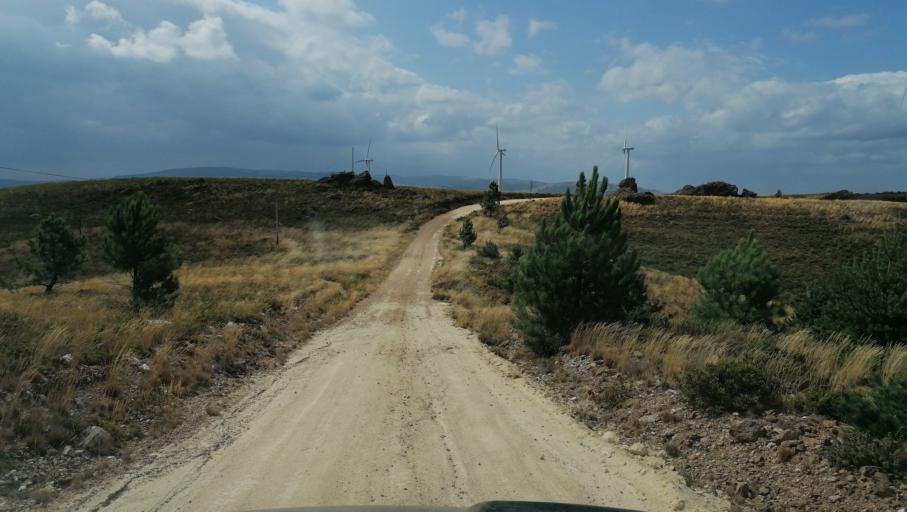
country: PT
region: Vila Real
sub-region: Vila Pouca de Aguiar
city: Vila Pouca de Aguiar
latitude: 41.5338
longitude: -7.7159
